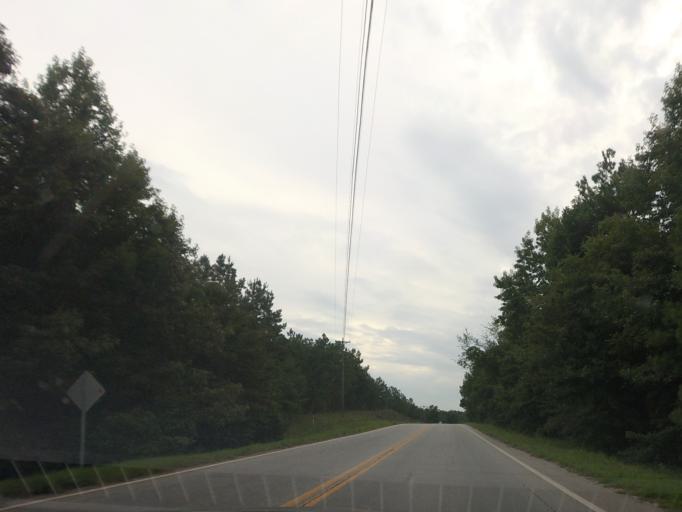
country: US
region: Georgia
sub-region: Twiggs County
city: Jeffersonville
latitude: 32.7655
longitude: -83.4747
